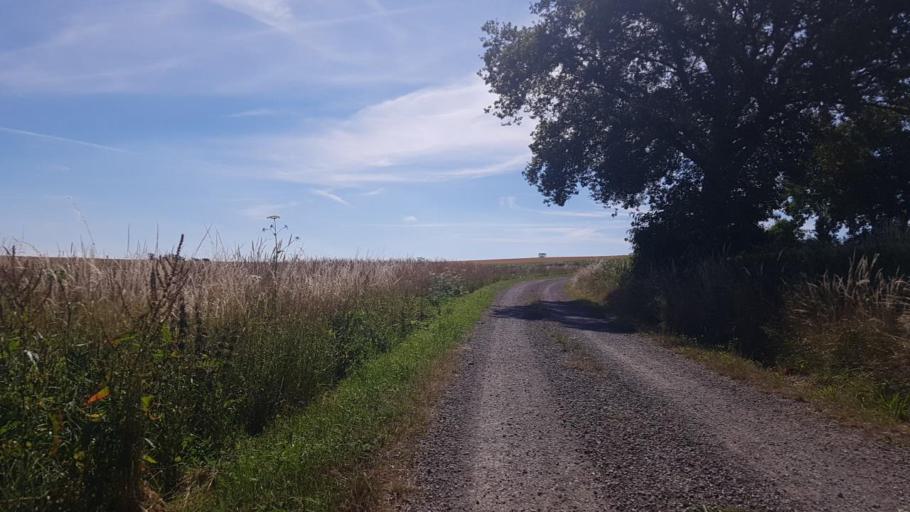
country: DE
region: North Rhine-Westphalia
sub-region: Regierungsbezirk Koln
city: Kall
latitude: 50.6196
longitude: 6.5536
